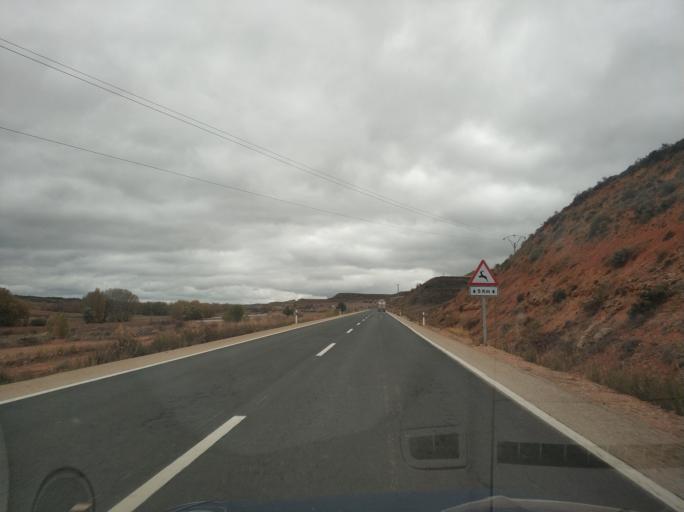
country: ES
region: Castille and Leon
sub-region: Provincia de Soria
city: San Esteban de Gormaz
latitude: 41.5797
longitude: -3.2232
